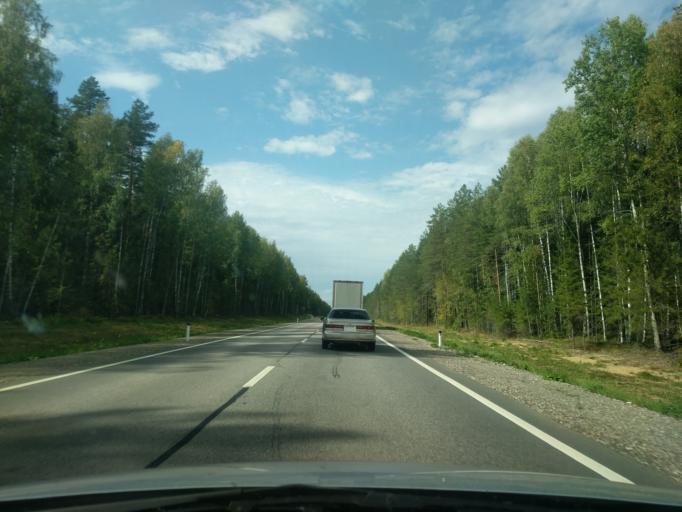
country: RU
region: Kostroma
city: Kadyy
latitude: 57.7968
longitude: 42.8426
